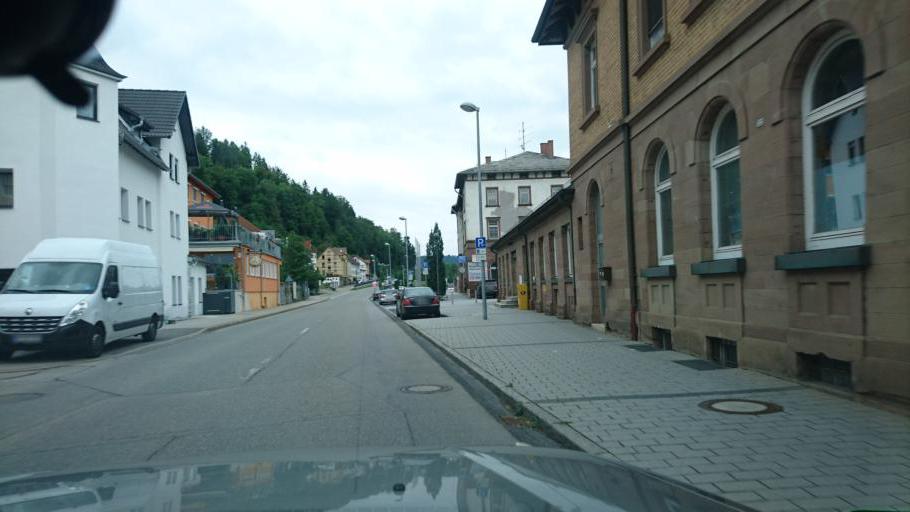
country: DE
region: Baden-Wuerttemberg
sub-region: Freiburg Region
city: Oberndorf
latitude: 48.2947
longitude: 8.5752
